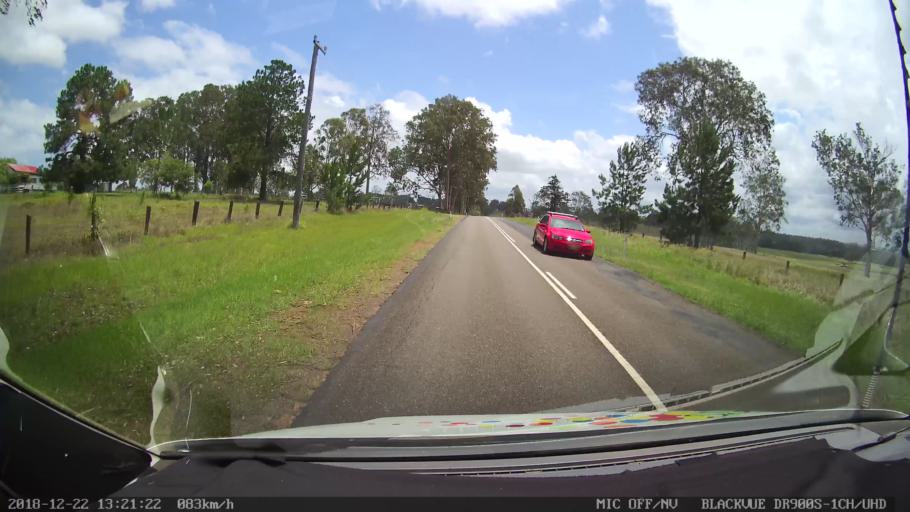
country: AU
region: New South Wales
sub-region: Clarence Valley
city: Coutts Crossing
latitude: -29.7762
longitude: 152.9210
